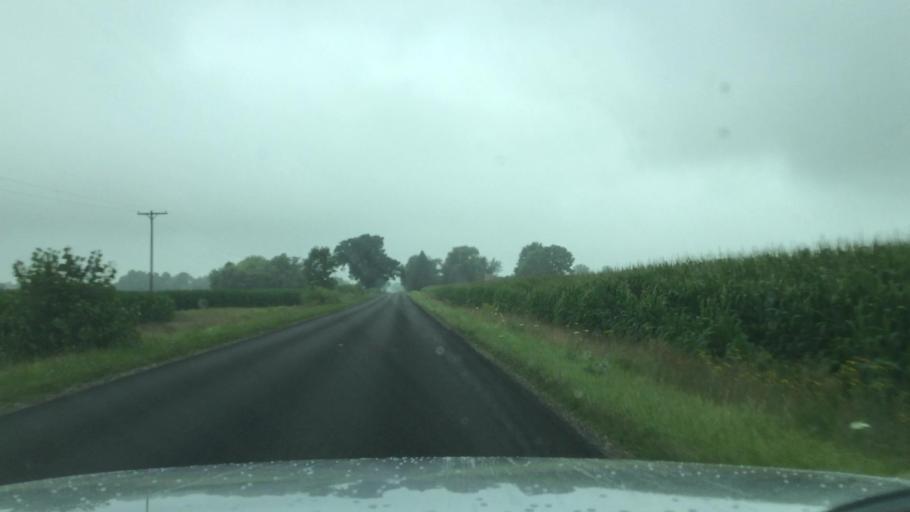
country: US
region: Michigan
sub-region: Shiawassee County
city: New Haven
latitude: 43.0574
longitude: -84.1418
